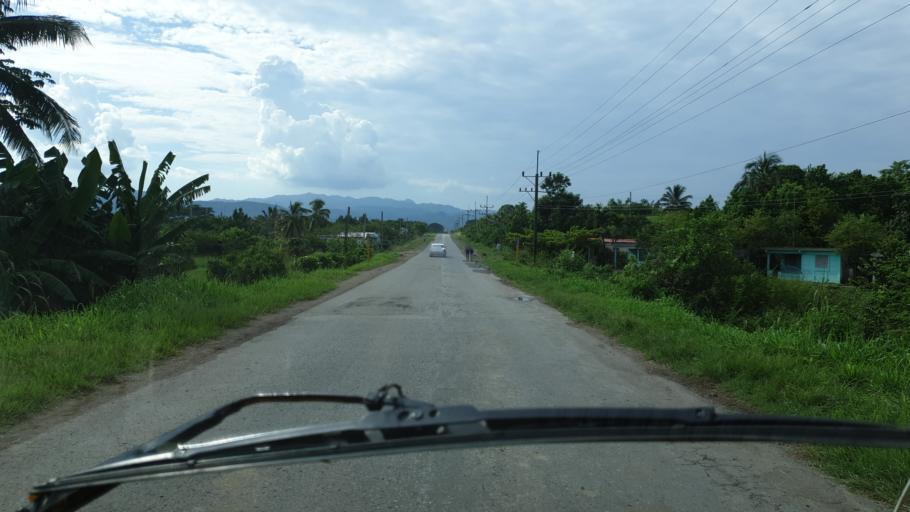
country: CU
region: Cienfuegos
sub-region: Municipio de Cienfuegos
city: Cumanayagua
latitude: 22.0746
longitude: -80.3106
